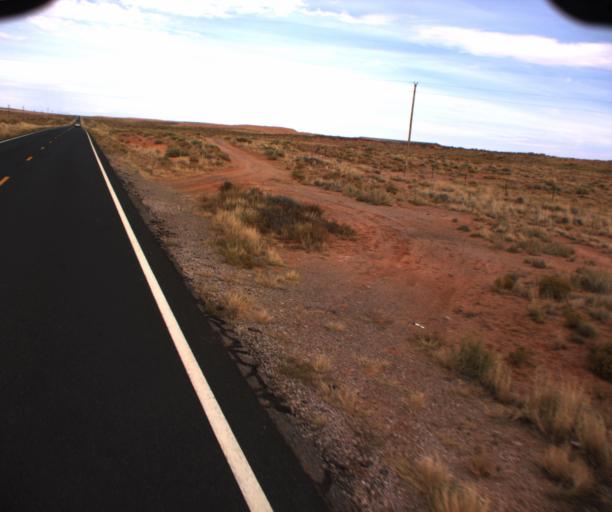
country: US
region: Arizona
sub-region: Apache County
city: Many Farms
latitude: 36.7950
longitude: -109.6497
